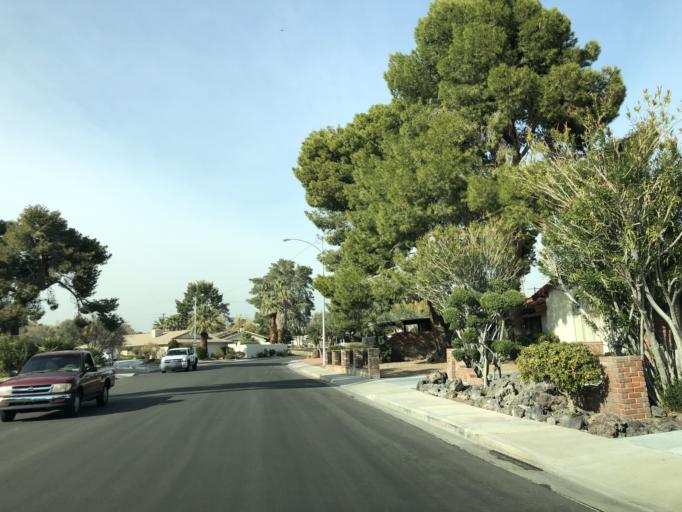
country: US
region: Nevada
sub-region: Clark County
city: Winchester
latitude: 36.1227
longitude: -115.1207
